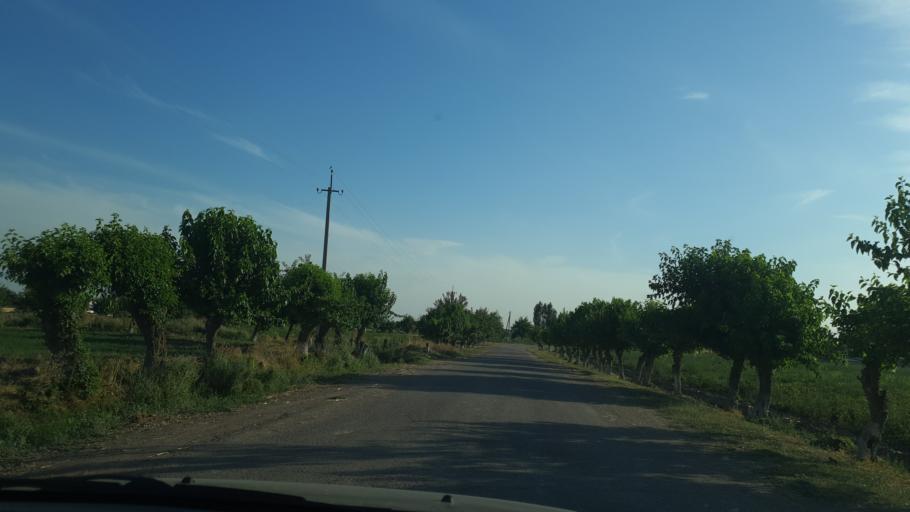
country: UZ
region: Toshkent
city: Tuytepa
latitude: 41.0917
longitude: 69.3692
